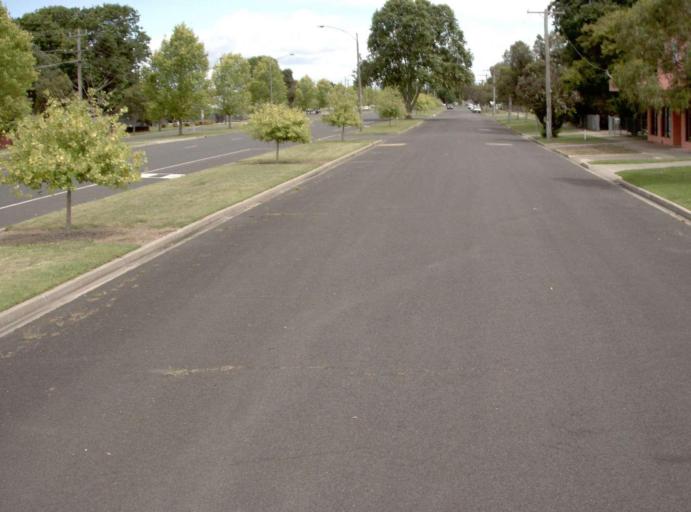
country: AU
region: Victoria
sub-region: Wellington
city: Sale
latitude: -37.9700
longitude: 146.9820
